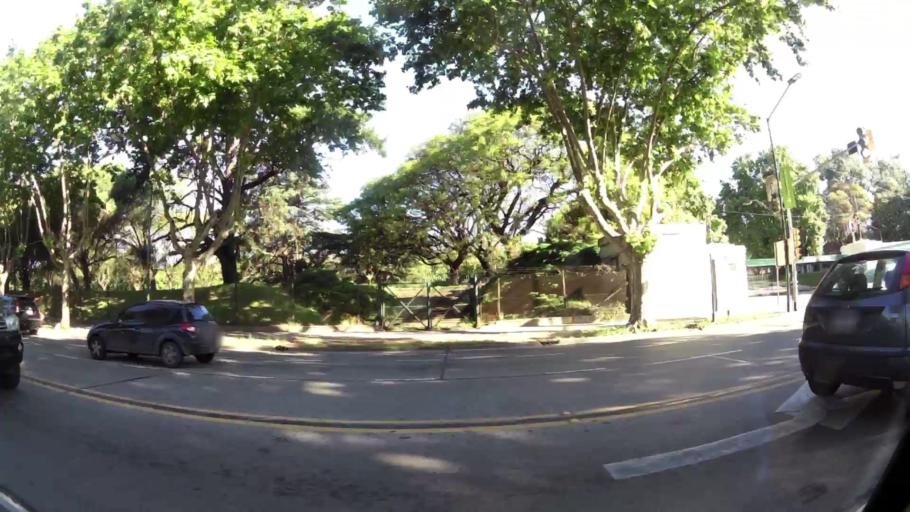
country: AR
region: Buenos Aires
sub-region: Partido de San Isidro
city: San Isidro
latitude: -34.4786
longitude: -58.5209
